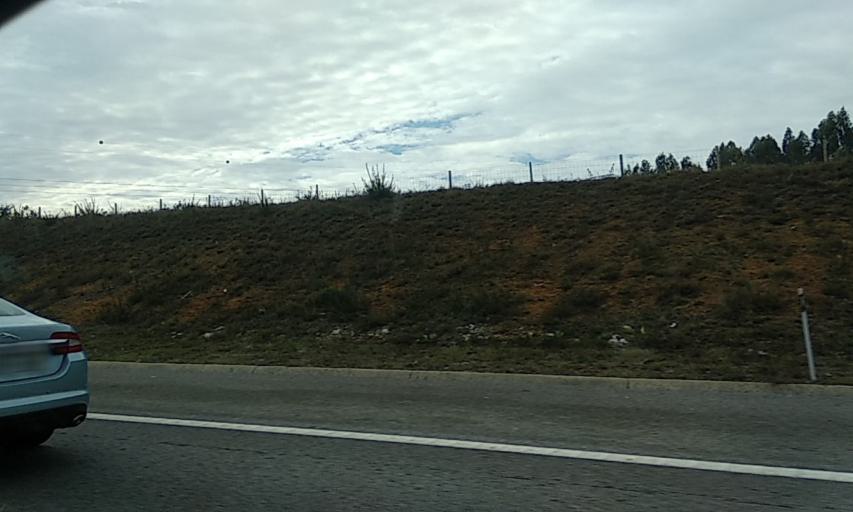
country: PT
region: Aveiro
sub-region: Estarreja
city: Beduido
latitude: 40.7871
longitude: -8.5476
